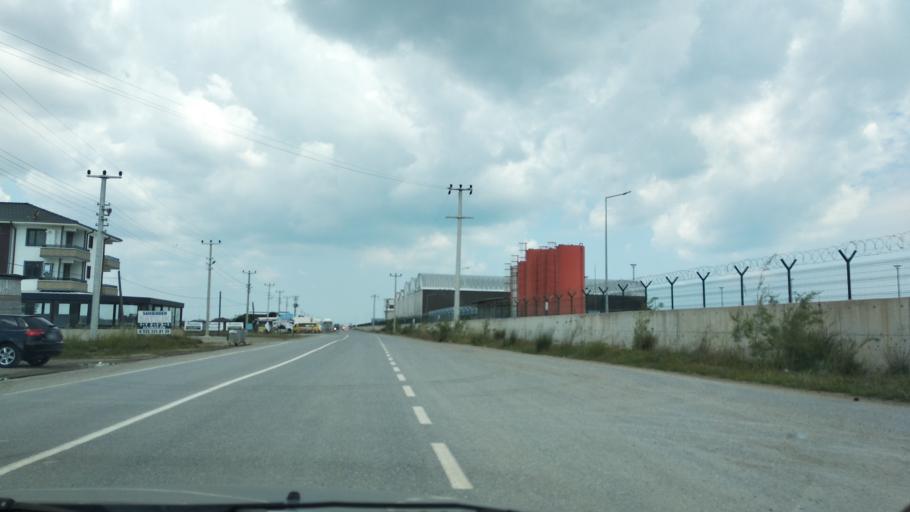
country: TR
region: Sakarya
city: Karasu
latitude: 41.1165
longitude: 30.6756
